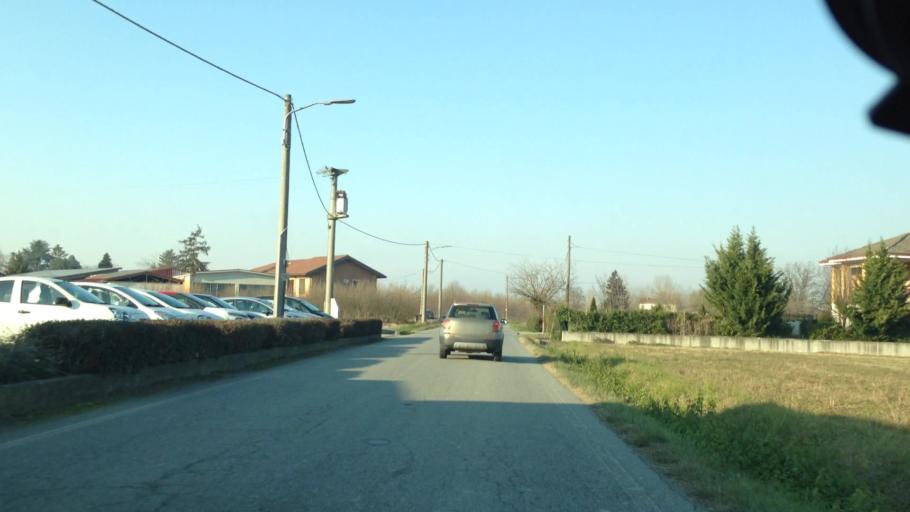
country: IT
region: Piedmont
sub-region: Provincia di Alessandria
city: Masio
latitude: 44.8676
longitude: 8.4205
